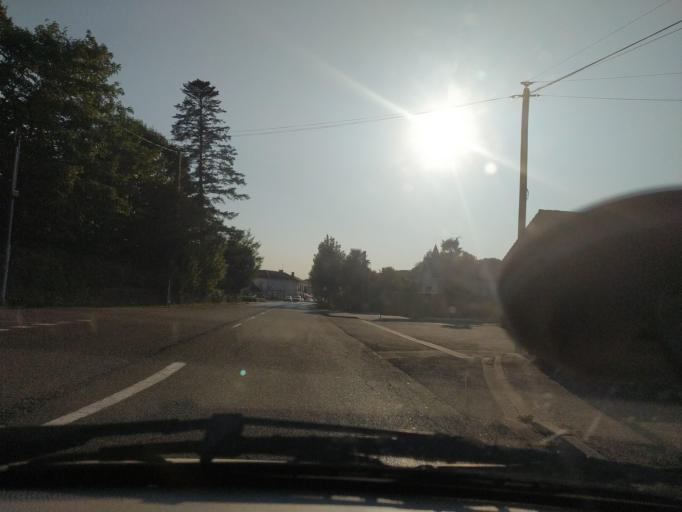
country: FR
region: Aquitaine
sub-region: Departement des Landes
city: Saint-Geours-de-Maremne
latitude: 43.6880
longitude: -1.2266
